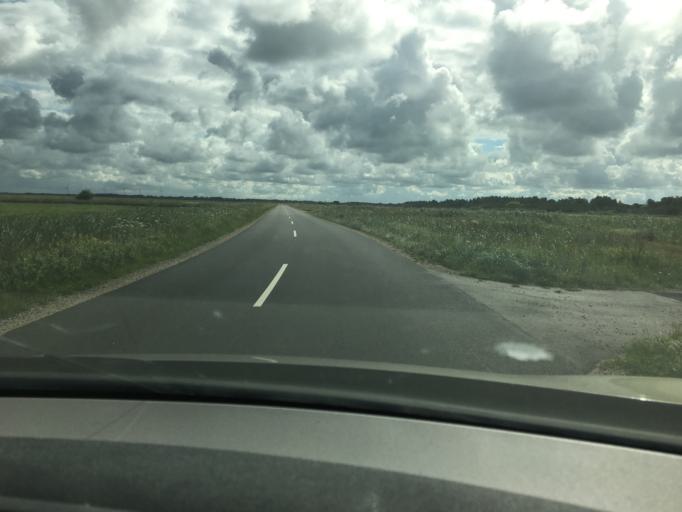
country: DK
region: Central Jutland
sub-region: Ringkobing-Skjern Kommune
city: Hvide Sande
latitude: 55.8287
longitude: 8.2334
